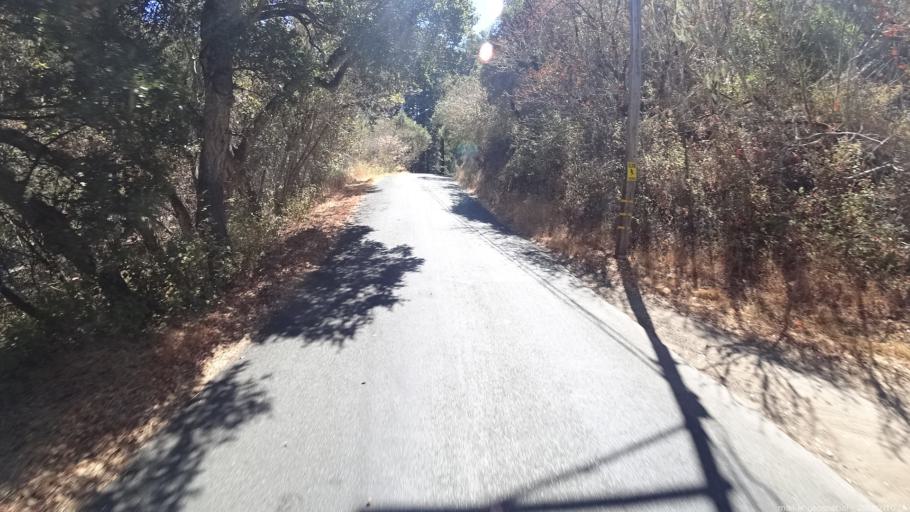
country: US
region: California
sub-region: Monterey County
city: Carmel Valley Village
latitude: 36.5157
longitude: -121.8130
